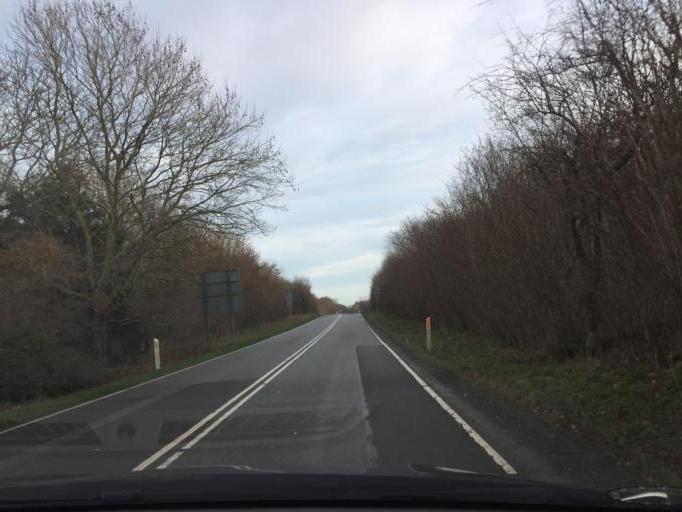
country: DK
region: South Denmark
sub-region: Faaborg-Midtfyn Kommune
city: Ringe
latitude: 55.2085
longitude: 10.4027
